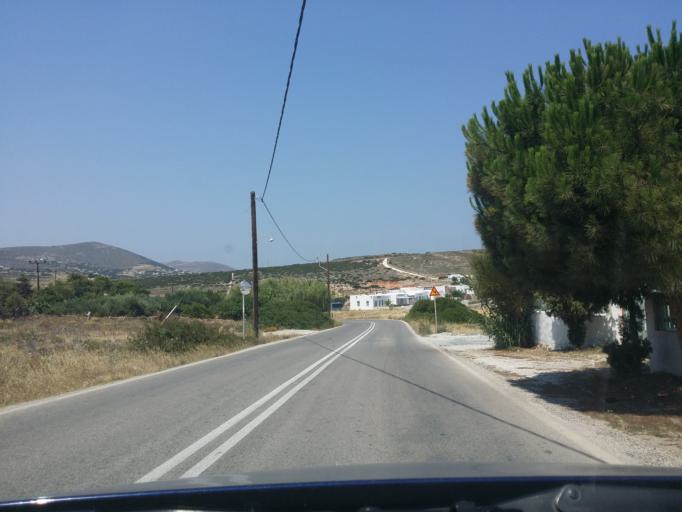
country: GR
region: South Aegean
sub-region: Nomos Kykladon
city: Naousa
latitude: 37.1165
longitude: 25.2380
